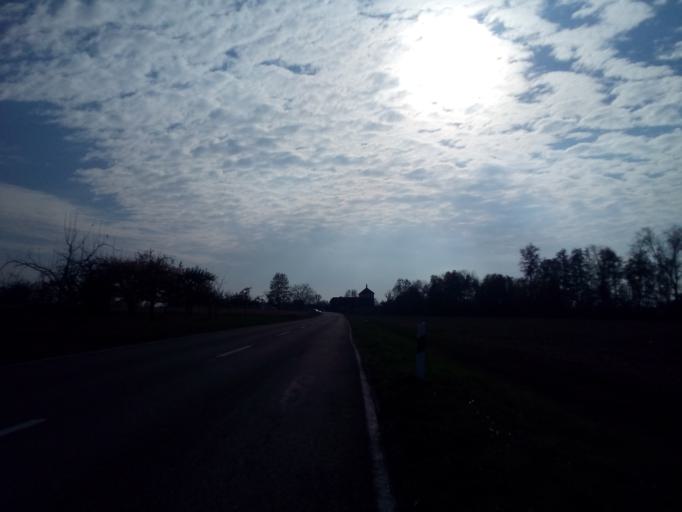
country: DE
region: Baden-Wuerttemberg
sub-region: Karlsruhe Region
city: Zell
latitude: 48.7003
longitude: 8.0677
